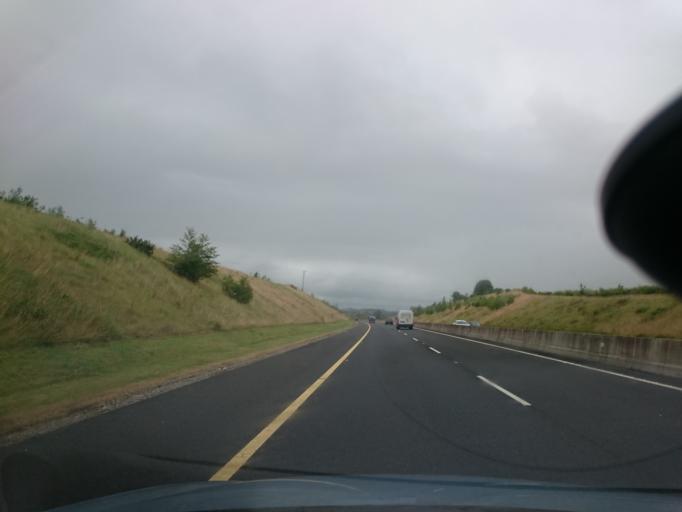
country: IE
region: Leinster
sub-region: Kildare
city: Castledermot
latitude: 52.9349
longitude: -6.8590
